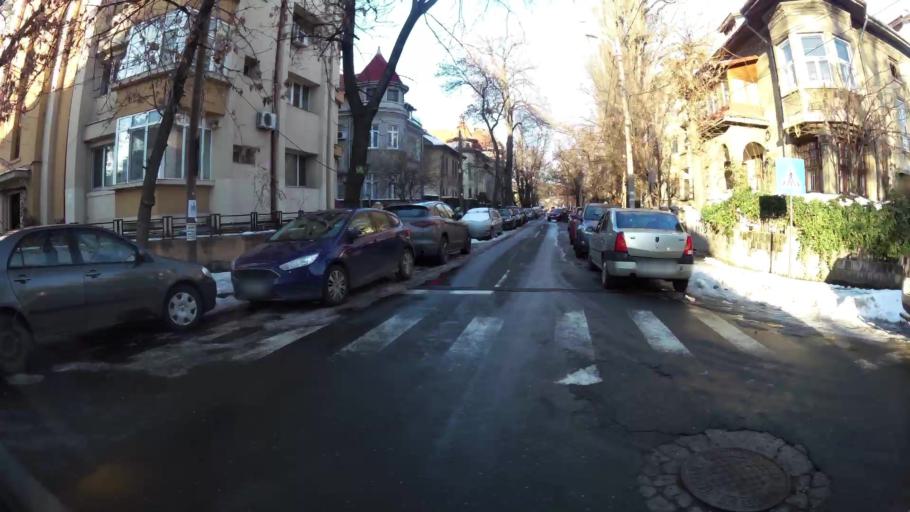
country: RO
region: Bucuresti
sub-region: Municipiul Bucuresti
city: Bucuresti
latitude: 44.4319
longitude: 26.0752
